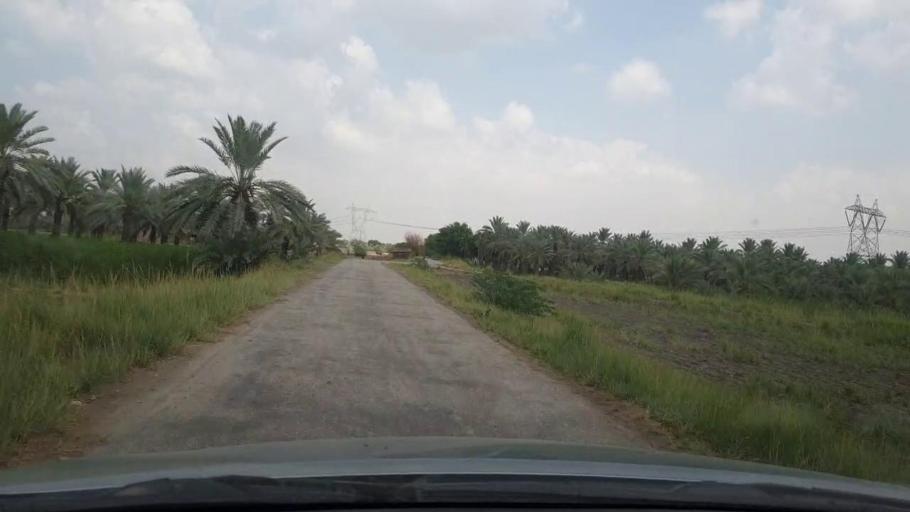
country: PK
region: Sindh
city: Khairpur
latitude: 27.4657
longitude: 68.7627
